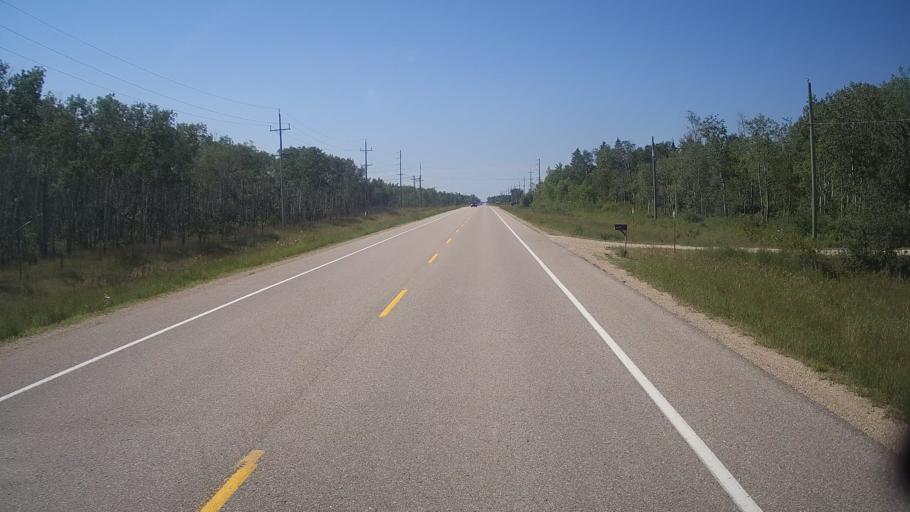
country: CA
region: Manitoba
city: La Broquerie
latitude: 49.6733
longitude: -96.4569
